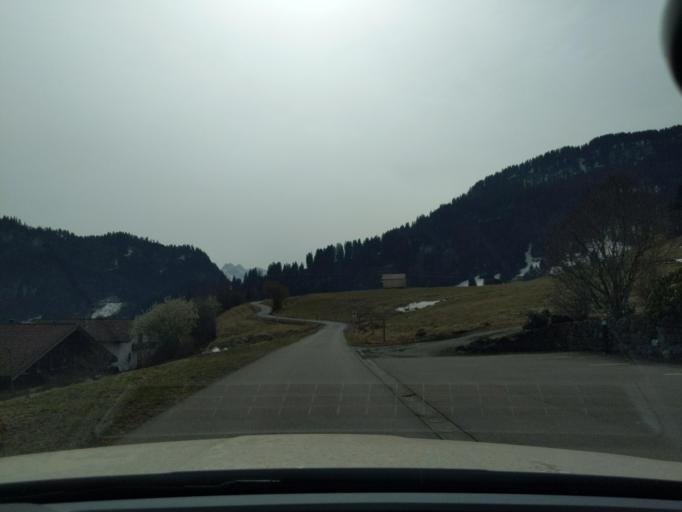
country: DE
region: Bavaria
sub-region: Swabia
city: Obermaiselstein
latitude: 47.4454
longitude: 10.2354
